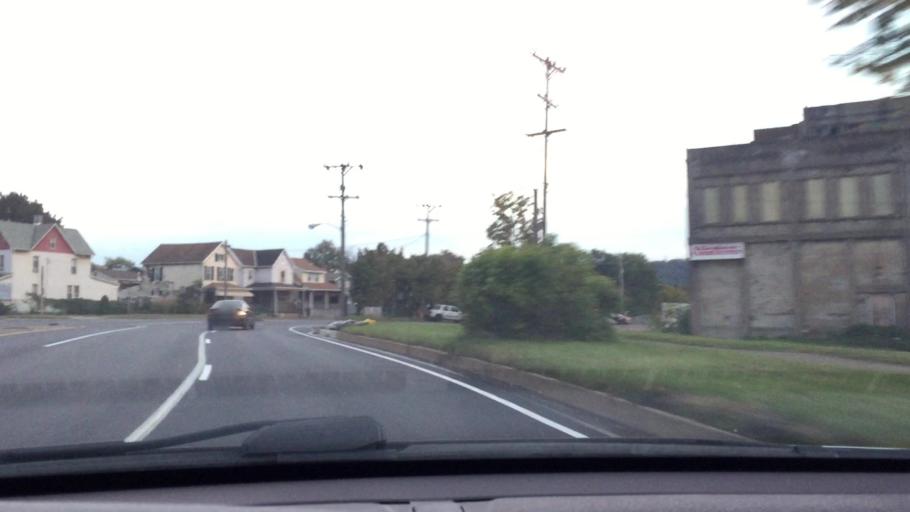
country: US
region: Pennsylvania
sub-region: Westmoreland County
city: New Kensington
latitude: 40.5610
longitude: -79.7672
